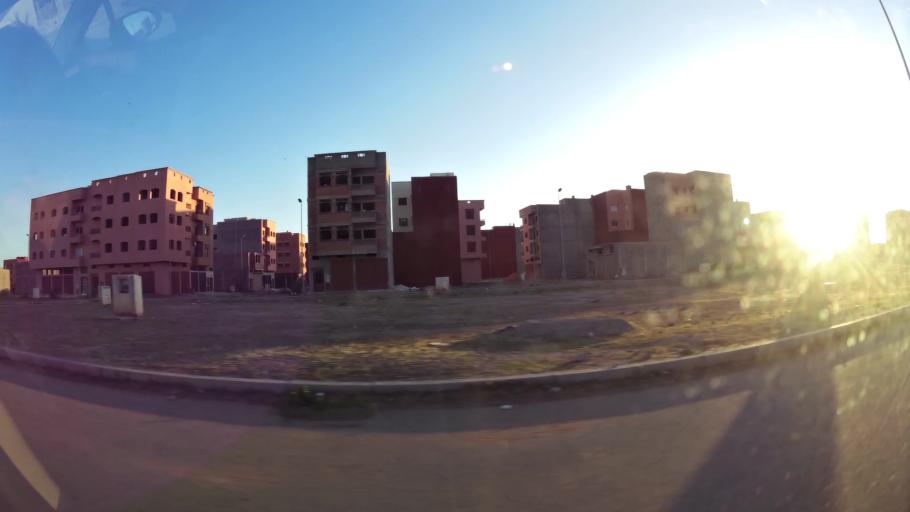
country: MA
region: Marrakech-Tensift-Al Haouz
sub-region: Kelaa-Des-Sraghna
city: Sidi Abdallah
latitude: 32.2384
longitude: -7.9449
